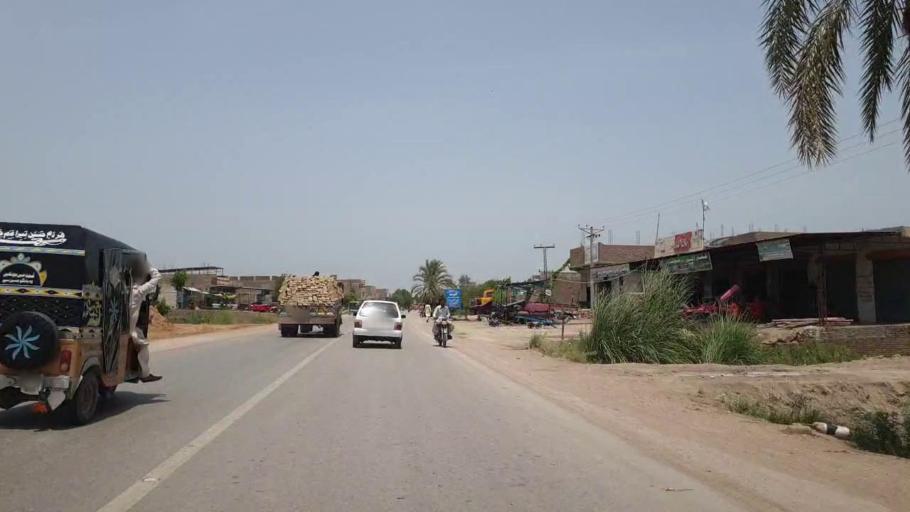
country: PK
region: Sindh
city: Nawabshah
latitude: 26.2457
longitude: 68.4357
